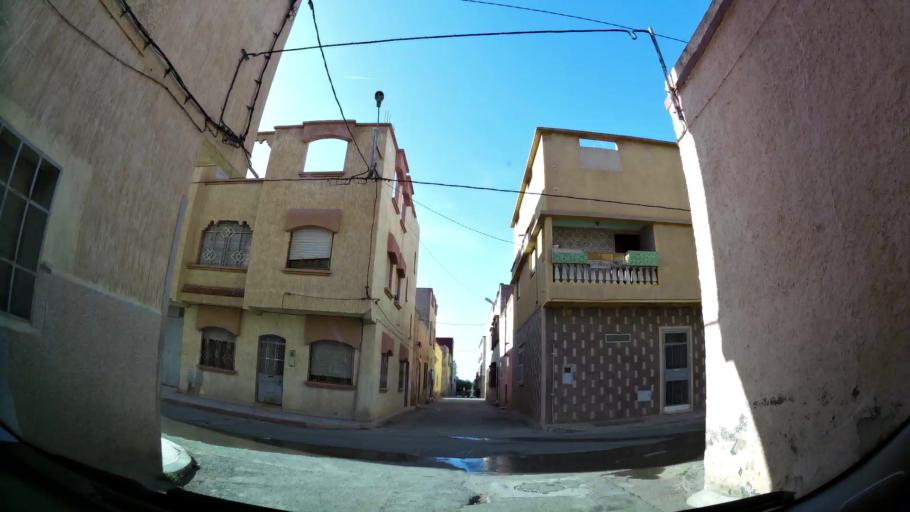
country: MA
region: Oriental
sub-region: Oujda-Angad
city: Oujda
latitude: 34.6951
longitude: -1.9180
